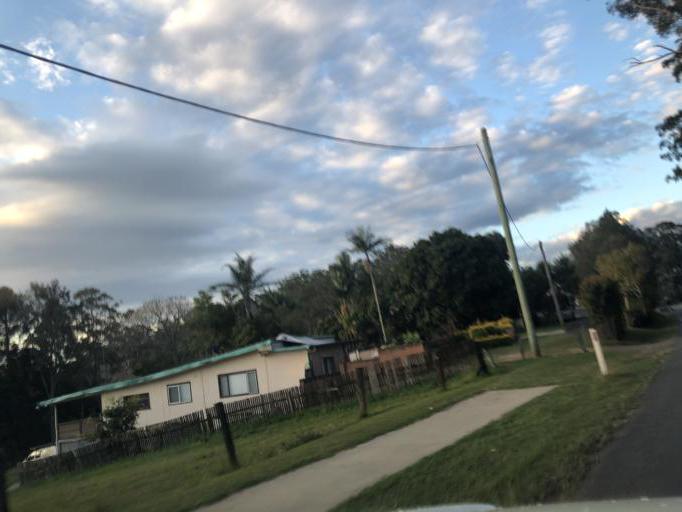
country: AU
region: New South Wales
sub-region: Nambucca Shire
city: Macksville
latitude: -30.7296
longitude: 152.9149
